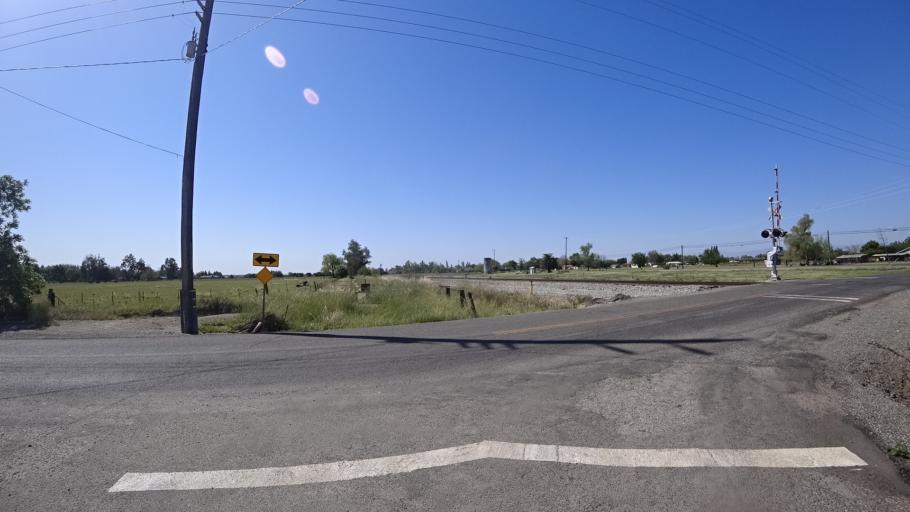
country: US
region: California
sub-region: Glenn County
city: Orland
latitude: 39.7258
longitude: -122.1959
